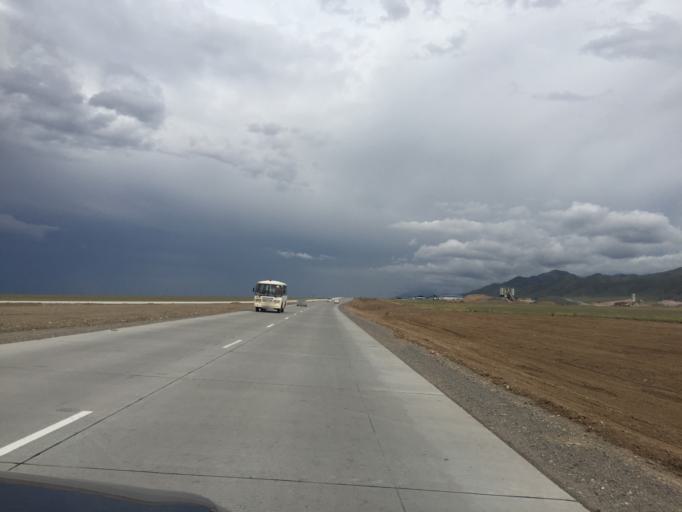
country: KG
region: Chuy
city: Ivanovka
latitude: 43.3934
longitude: 75.1331
